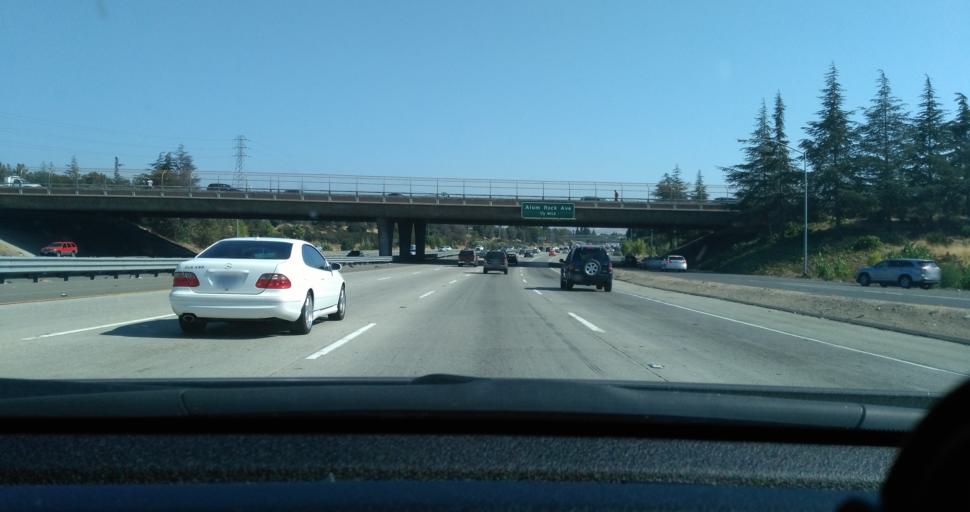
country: US
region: California
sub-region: Santa Clara County
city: Alum Rock
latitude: 37.3688
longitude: -121.8471
